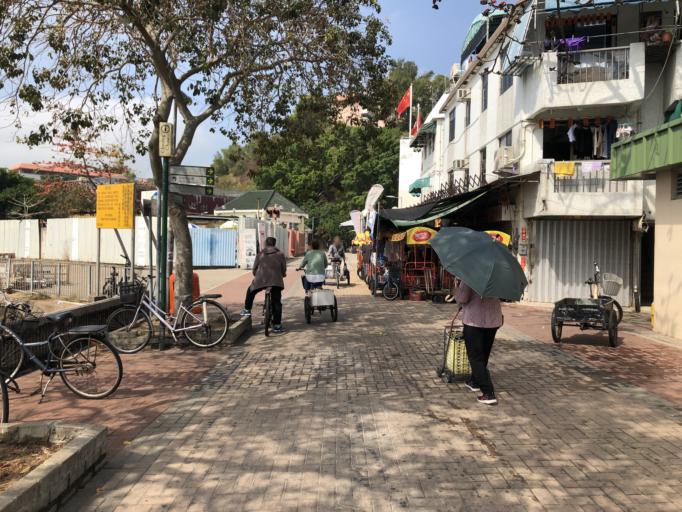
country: HK
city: Yung Shue Wan
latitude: 22.2118
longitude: 114.0266
